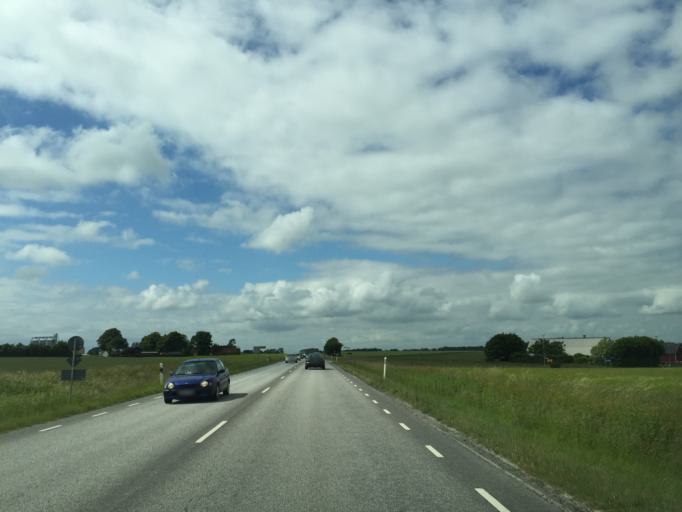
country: SE
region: Skane
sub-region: Staffanstorps Kommun
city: Staffanstorp
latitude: 55.6666
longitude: 13.2019
